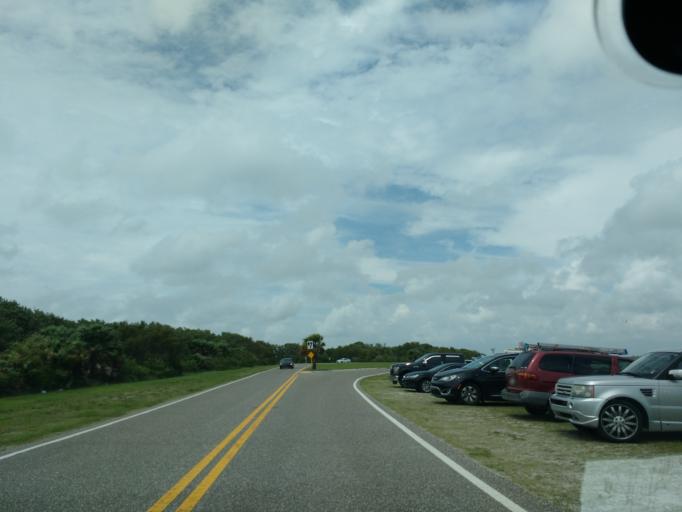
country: US
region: Florida
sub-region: Pinellas County
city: Tierra Verde
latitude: 27.6363
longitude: -82.6999
